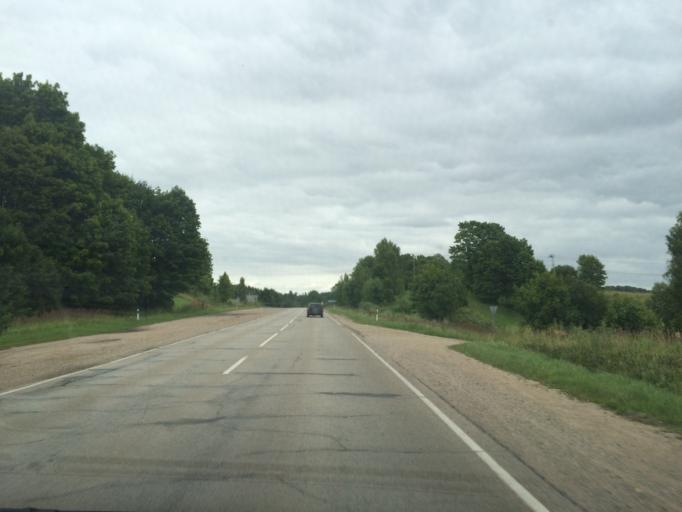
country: LV
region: Rezekne
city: Rezekne
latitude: 56.5850
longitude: 27.3986
